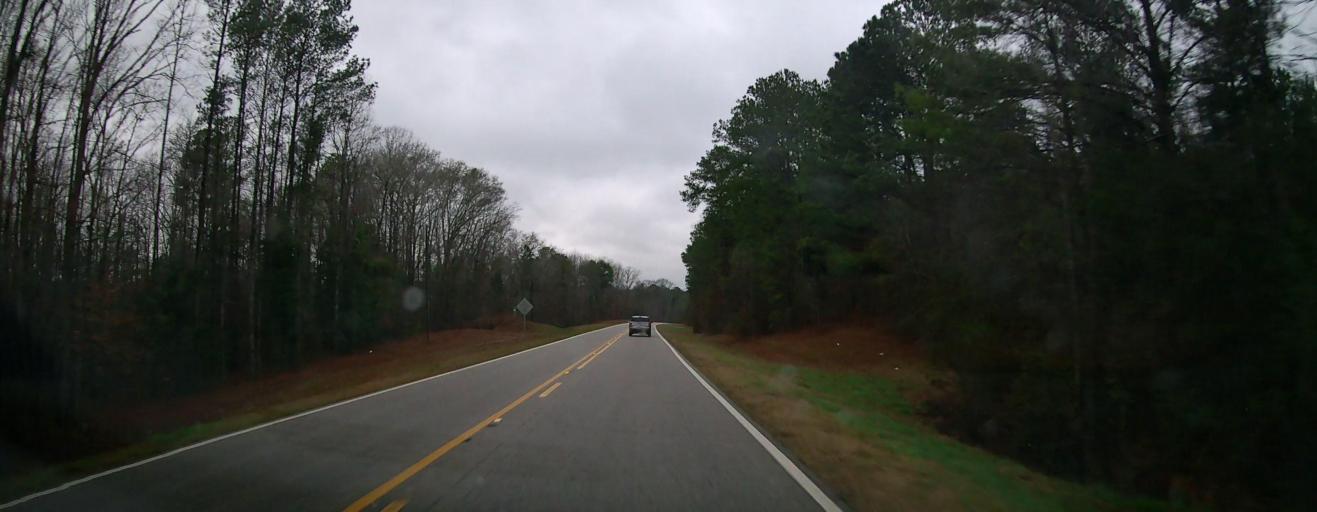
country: US
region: Alabama
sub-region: Bibb County
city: Centreville
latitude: 32.9058
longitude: -87.0121
